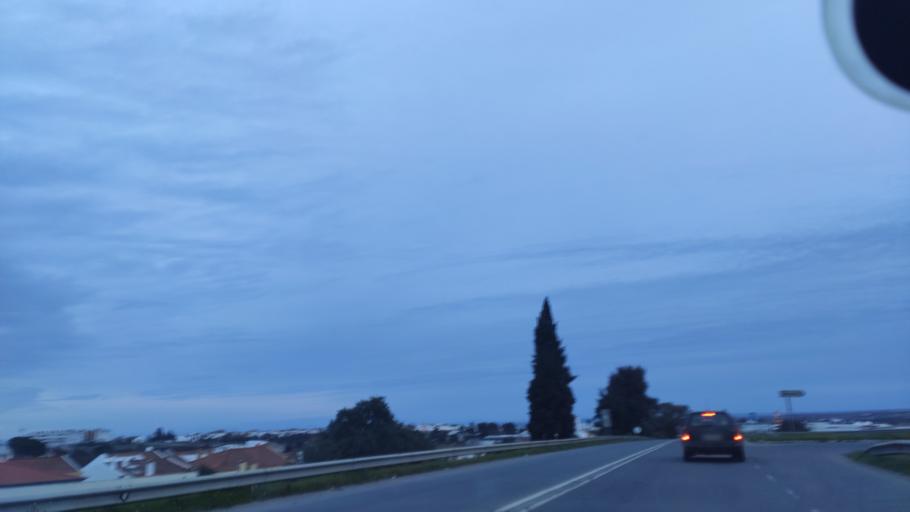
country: PT
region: Beja
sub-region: Beja
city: Beja
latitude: 38.0245
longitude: -7.8591
